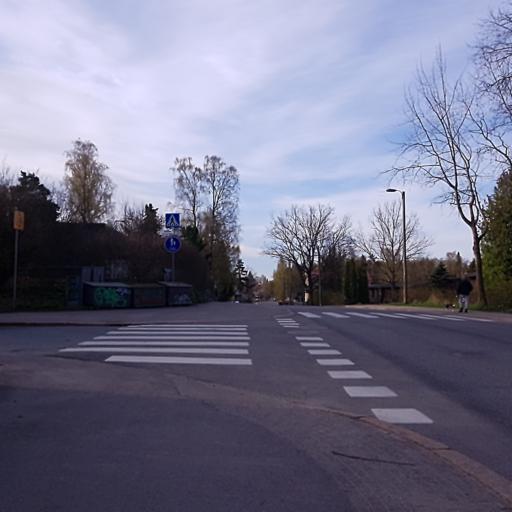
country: FI
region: Uusimaa
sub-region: Helsinki
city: Helsinki
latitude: 60.2485
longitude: 24.9425
